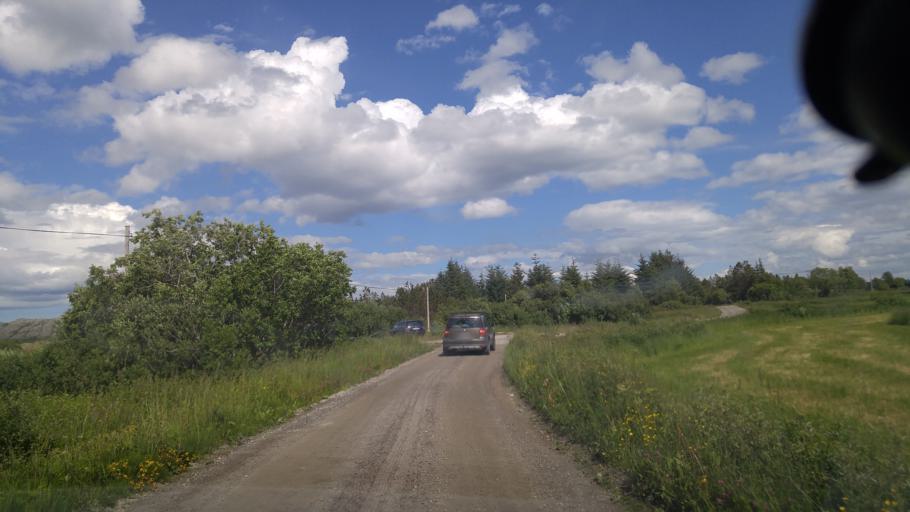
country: NO
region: Nord-Trondelag
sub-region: Vikna
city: Rorvik
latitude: 64.8973
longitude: 11.1112
